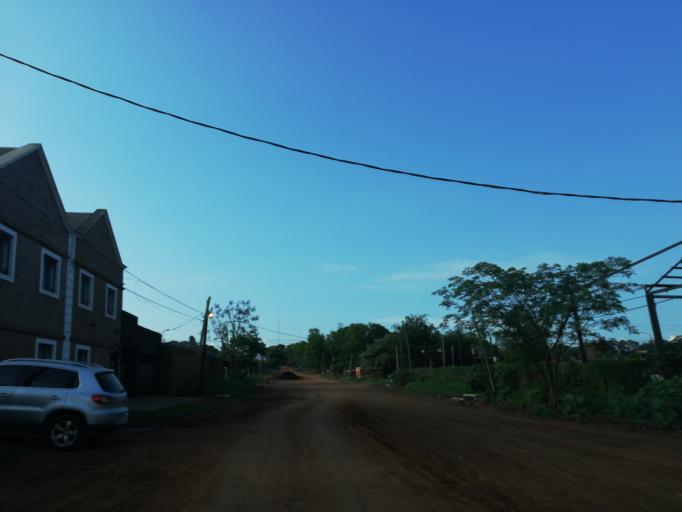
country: AR
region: Misiones
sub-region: Departamento de Capital
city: Posadas
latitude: -27.3978
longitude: -55.9245
